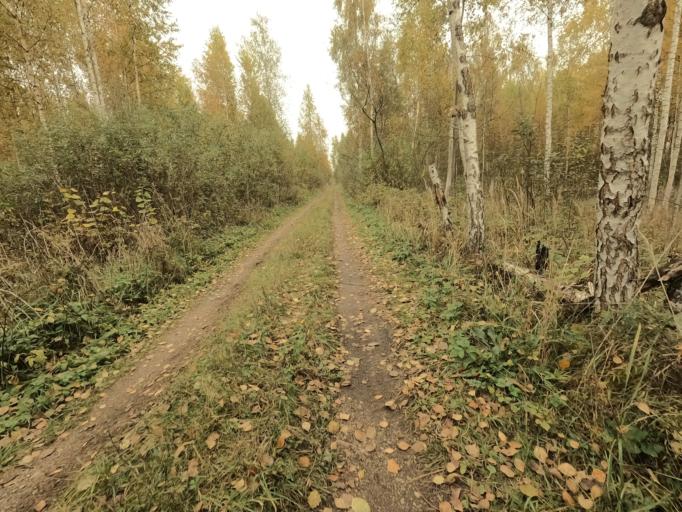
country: RU
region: Novgorod
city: Pankovka
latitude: 58.8722
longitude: 30.9377
